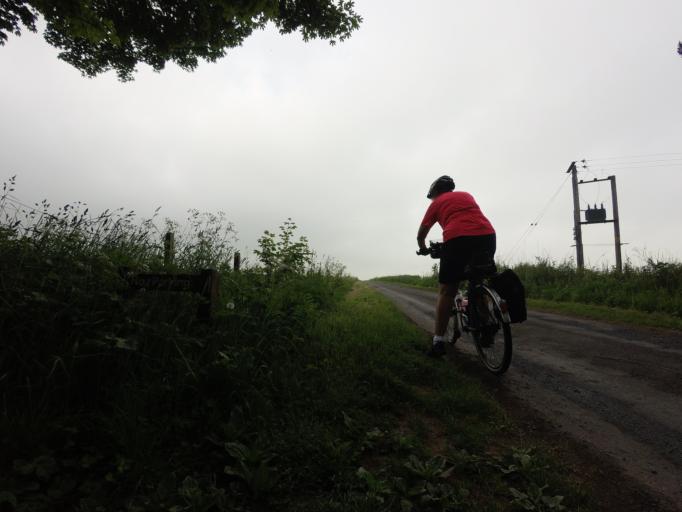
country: GB
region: Scotland
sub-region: Perth and Kinross
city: Milnathort
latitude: 56.2461
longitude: -3.3390
